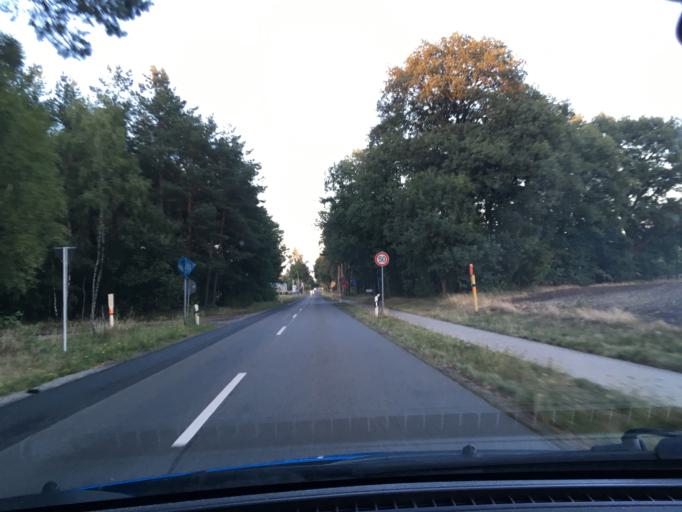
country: DE
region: Lower Saxony
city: Fassberg
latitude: 52.8916
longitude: 10.1530
